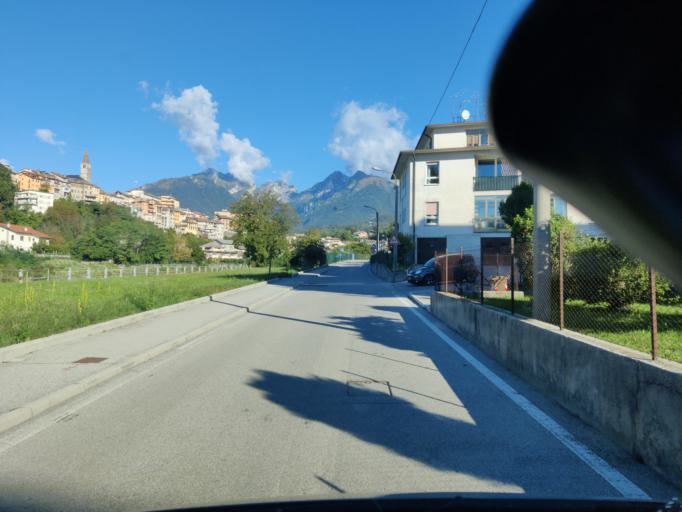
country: IT
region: Veneto
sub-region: Provincia di Belluno
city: Belluno
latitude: 46.1390
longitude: 12.2225
